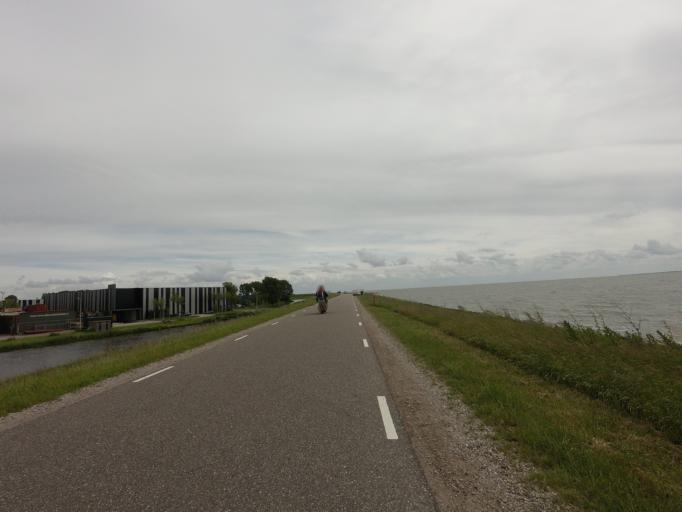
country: NL
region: North Holland
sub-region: Gemeente Hoorn
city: Hoorn
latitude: 52.6375
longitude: 5.0971
